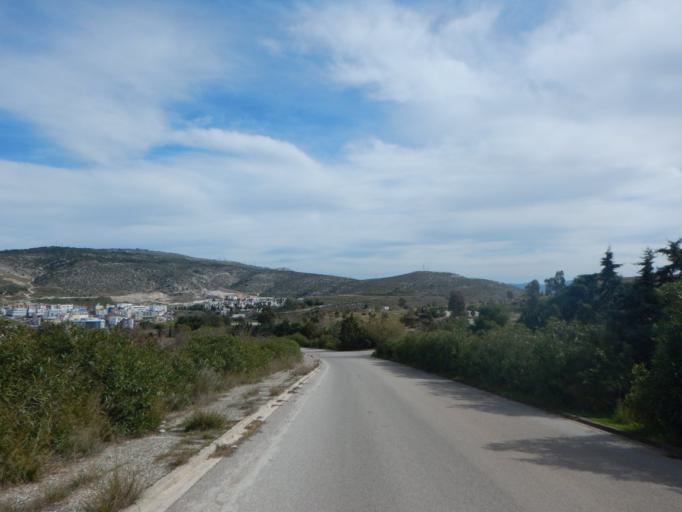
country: GR
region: Attica
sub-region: Nomos Piraios
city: Perama
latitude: 37.9730
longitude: 23.5898
